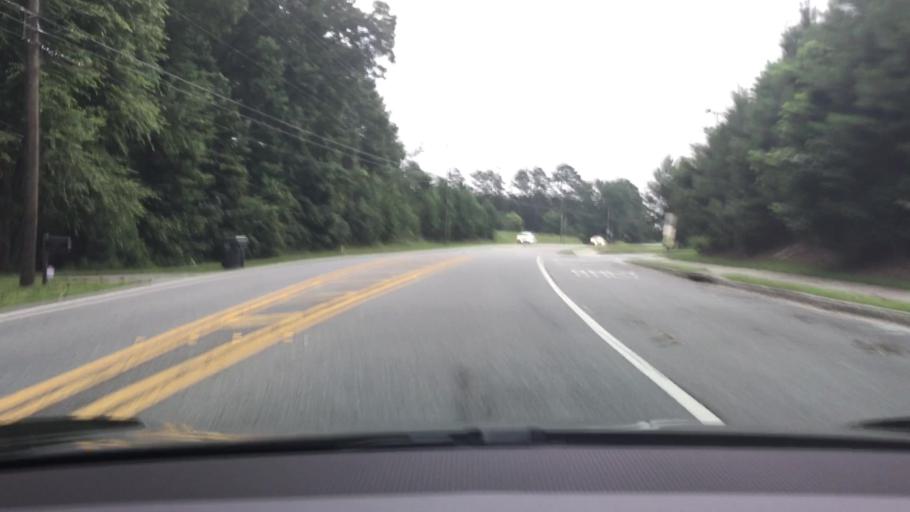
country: US
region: Georgia
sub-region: Gwinnett County
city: Suwanee
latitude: 34.0818
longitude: -84.0616
